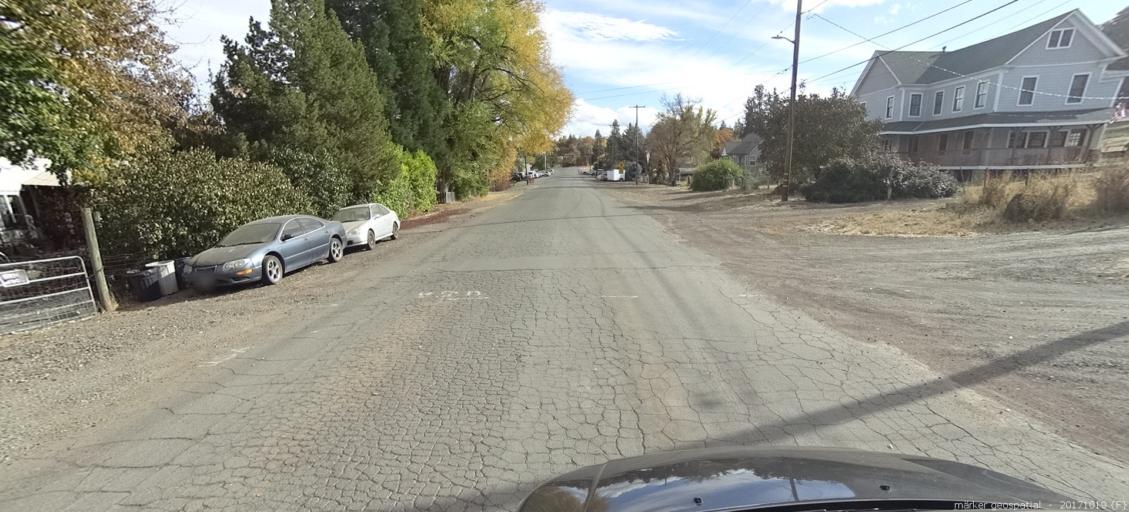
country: US
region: California
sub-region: Shasta County
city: Burney
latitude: 41.0044
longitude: -121.4443
